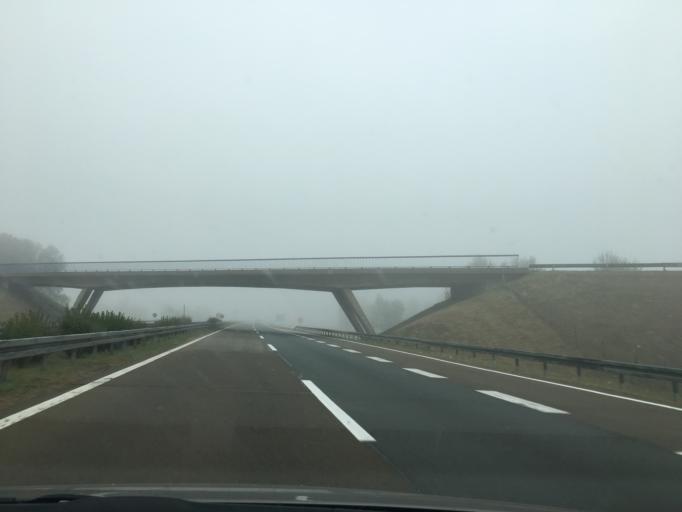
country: RS
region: Autonomna Pokrajina Vojvodina
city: Nova Pazova
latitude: 44.9859
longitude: 20.2159
